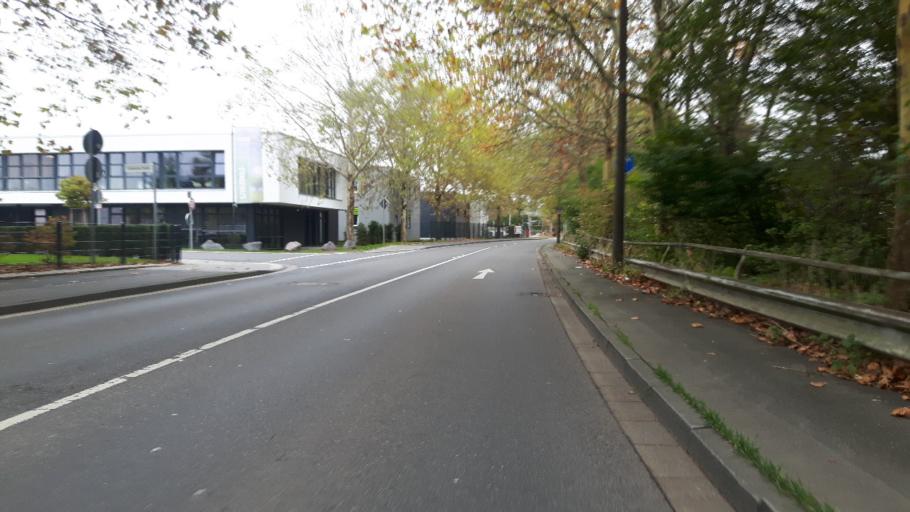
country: DE
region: North Rhine-Westphalia
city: Sankt Augustin
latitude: 50.7510
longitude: 7.1541
